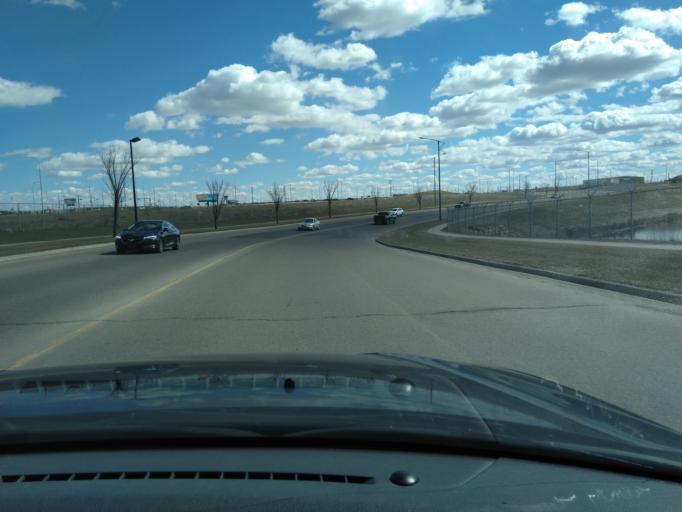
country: CA
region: Alberta
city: Calgary
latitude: 51.1388
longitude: -114.0178
